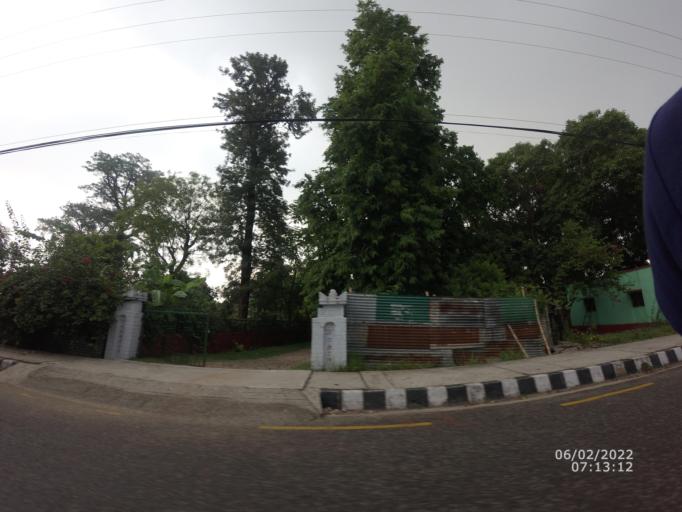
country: NP
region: Western Region
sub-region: Lumbini Zone
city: Bhairahawa
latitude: 27.4825
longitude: 83.4422
